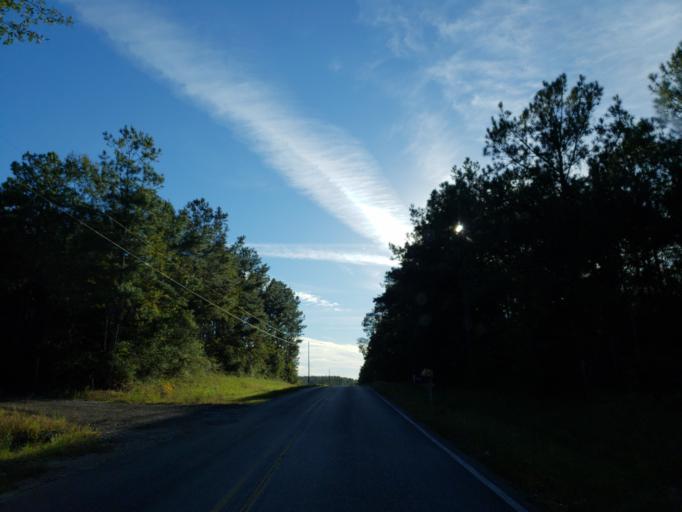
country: US
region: Mississippi
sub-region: Perry County
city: Richton
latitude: 31.3473
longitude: -88.7815
